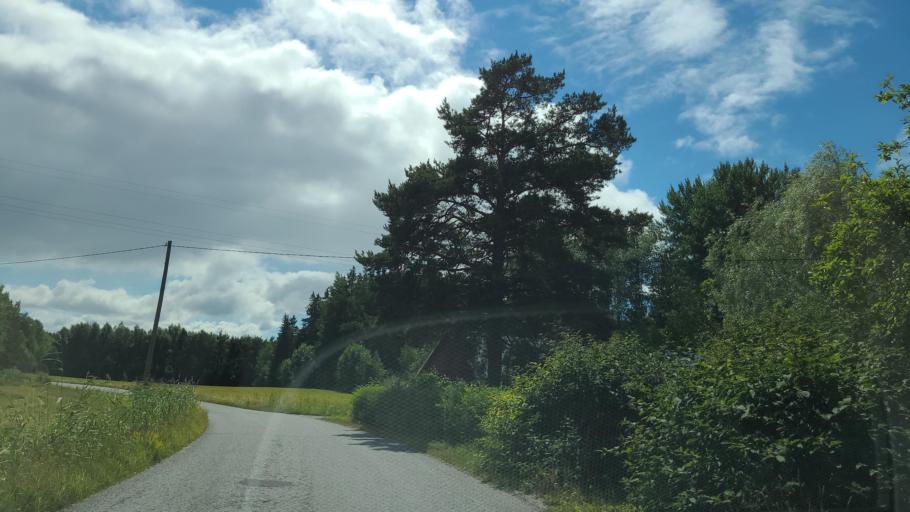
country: FI
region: Varsinais-Suomi
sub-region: Aboland-Turunmaa
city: Nagu
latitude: 60.1793
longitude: 22.0193
